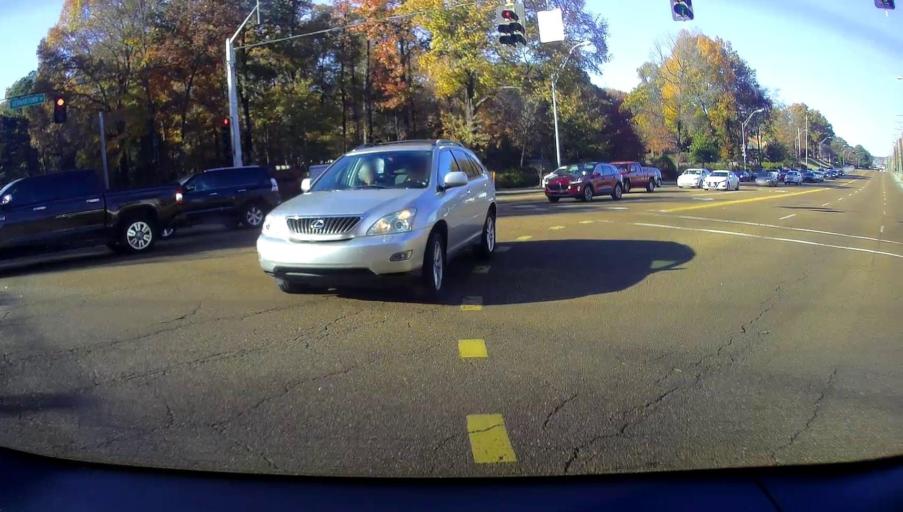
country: US
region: Tennessee
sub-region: Shelby County
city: Germantown
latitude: 35.1017
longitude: -89.8051
